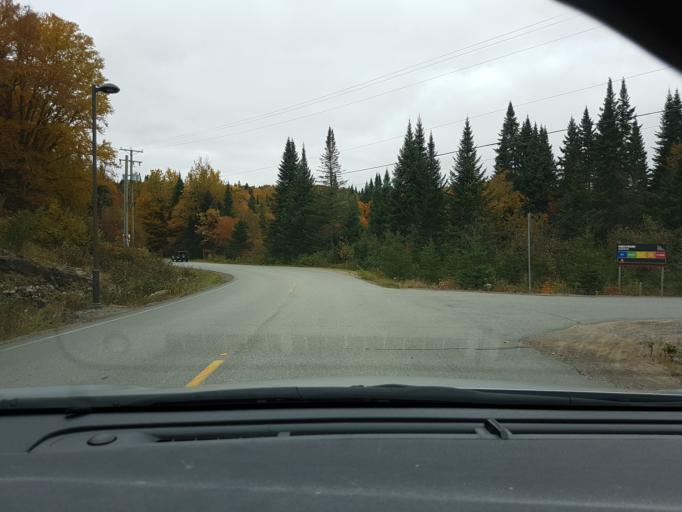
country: CA
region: Quebec
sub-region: Capitale-Nationale
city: Shannon
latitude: 47.1096
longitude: -71.3470
